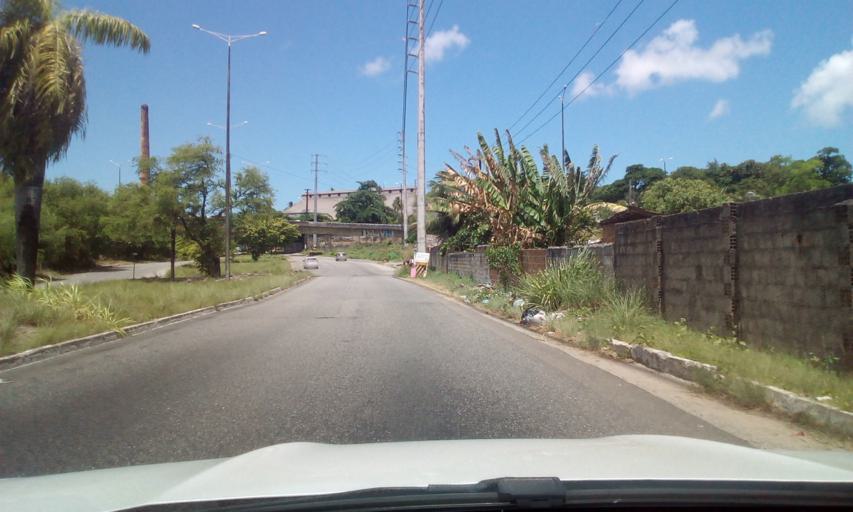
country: BR
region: Paraiba
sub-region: Joao Pessoa
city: Joao Pessoa
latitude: -7.1245
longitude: -34.8948
